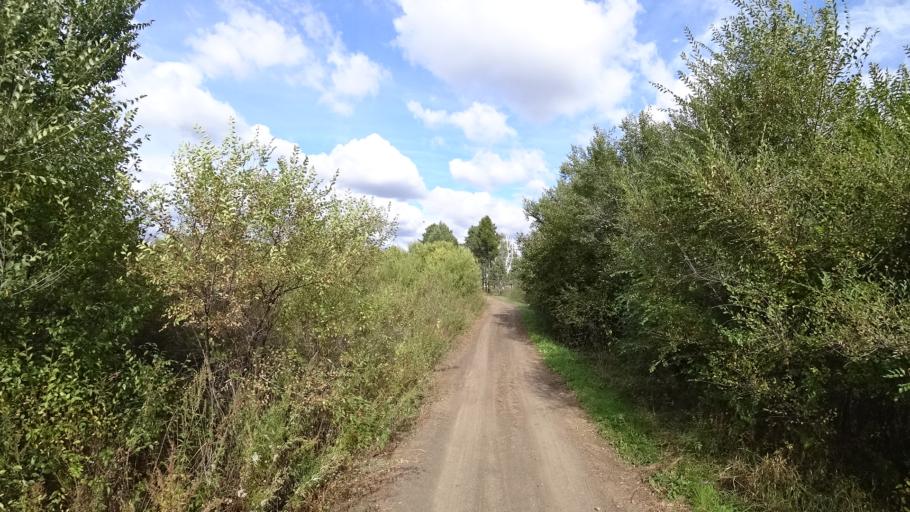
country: RU
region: Amur
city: Arkhara
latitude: 49.3515
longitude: 130.1601
